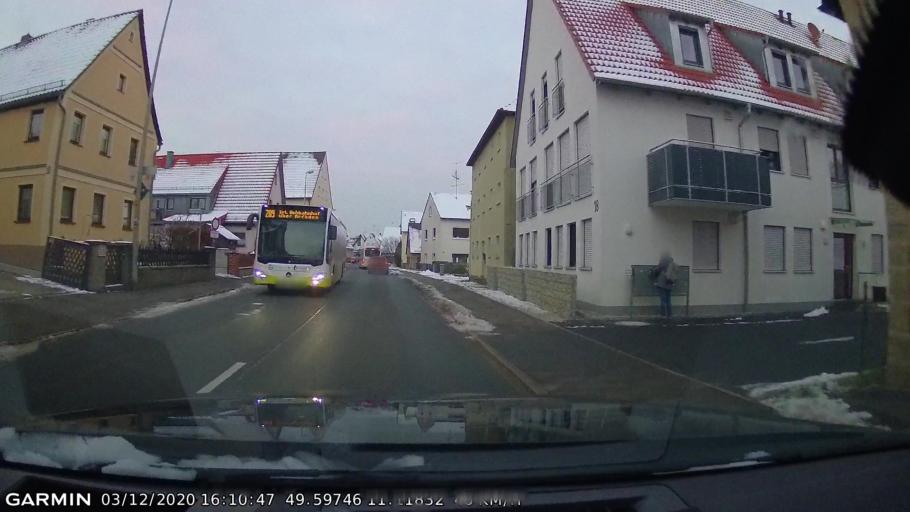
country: DE
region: Bavaria
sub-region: Upper Franconia
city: Dormitz
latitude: 49.5974
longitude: 11.1186
